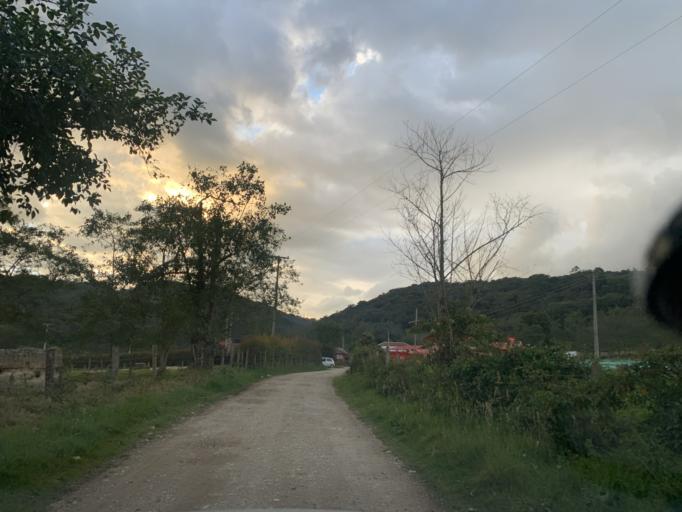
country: CO
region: Boyaca
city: La Capilla
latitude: 5.7379
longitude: -73.5054
